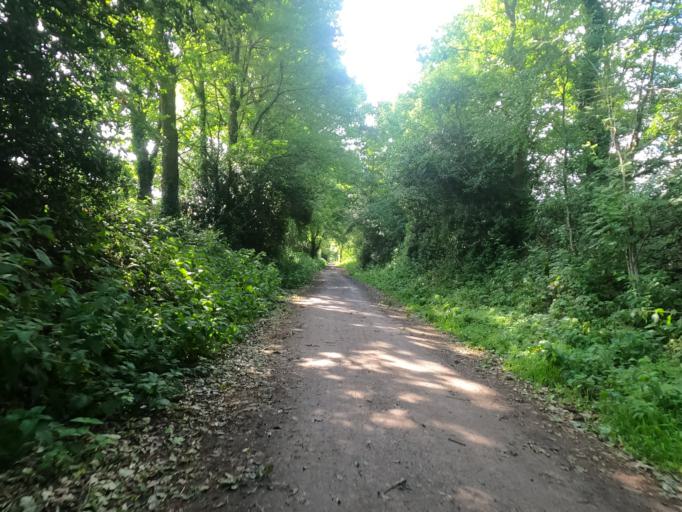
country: GB
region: England
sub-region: Cheshire West and Chester
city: Cuddington
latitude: 53.2098
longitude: -2.5848
